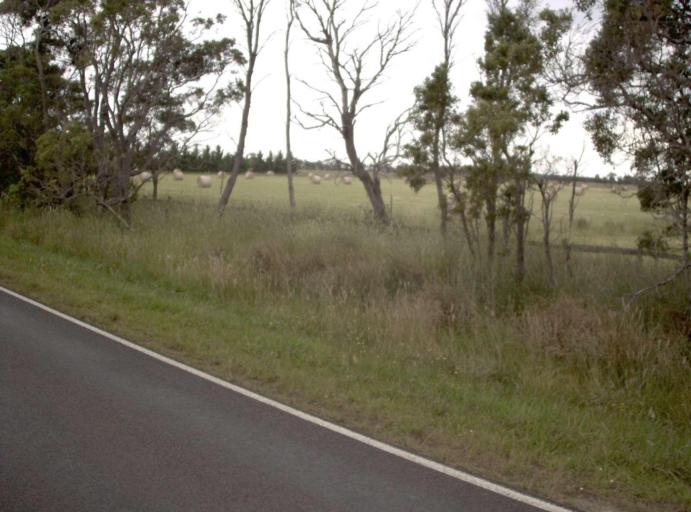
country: AU
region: Victoria
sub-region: Latrobe
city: Traralgon
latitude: -38.5498
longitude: 146.7258
